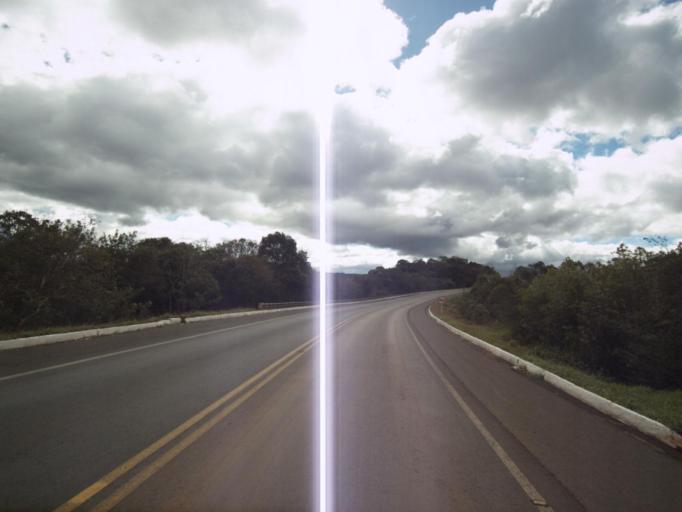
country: BR
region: Santa Catarina
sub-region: Concordia
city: Concordia
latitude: -27.3414
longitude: -51.9855
